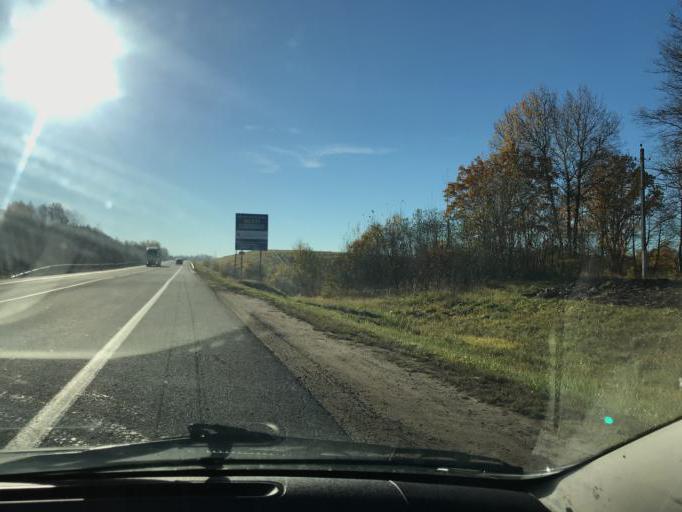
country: BY
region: Vitebsk
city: Vitebsk
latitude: 55.0959
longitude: 30.3015
